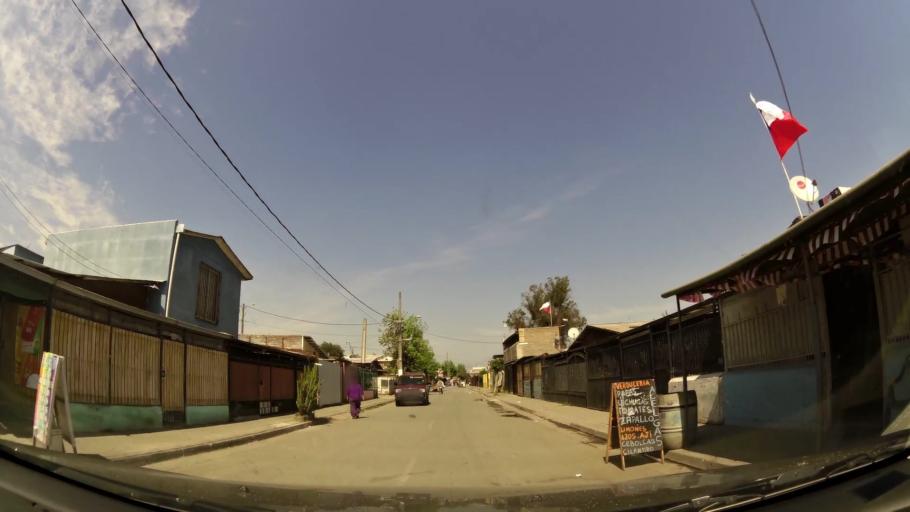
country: CL
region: Santiago Metropolitan
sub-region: Provincia de Santiago
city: La Pintana
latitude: -33.5906
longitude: -70.6099
